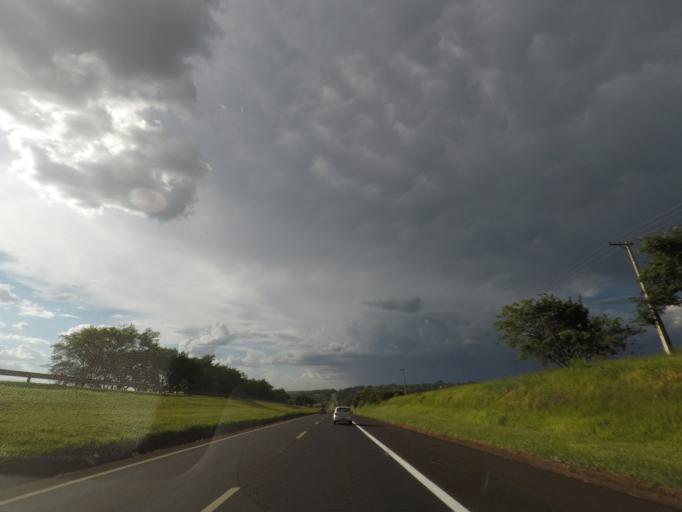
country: BR
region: Sao Paulo
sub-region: Jardinopolis
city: Jardinopolis
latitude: -21.0767
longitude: -47.8063
